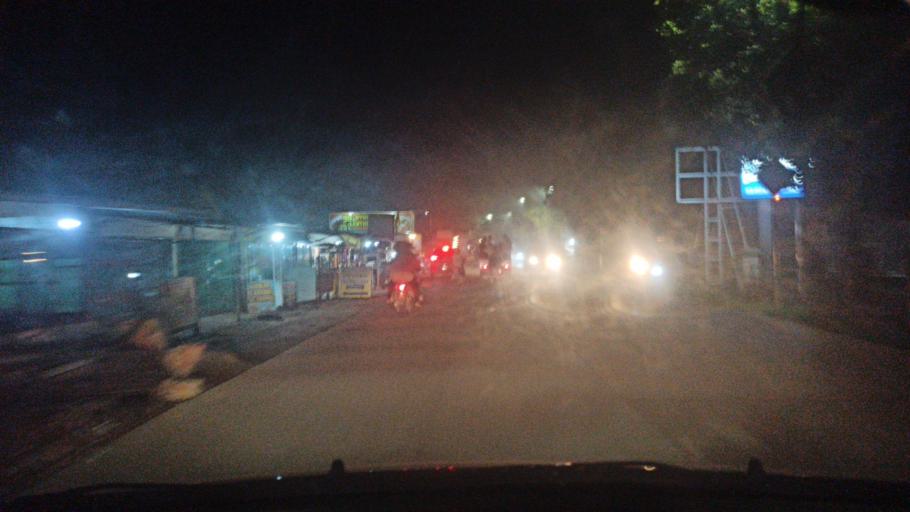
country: ID
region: South Sumatra
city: Plaju
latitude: -2.9461
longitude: 104.7854
